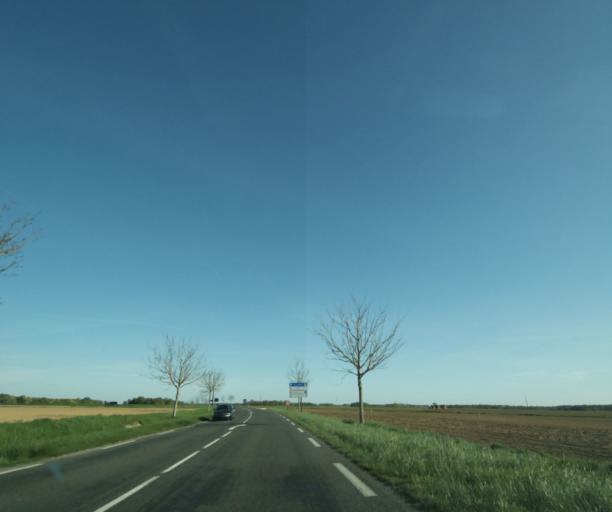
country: FR
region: Ile-de-France
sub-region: Departement de Seine-et-Marne
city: Nangis
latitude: 48.5519
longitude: 2.9987
